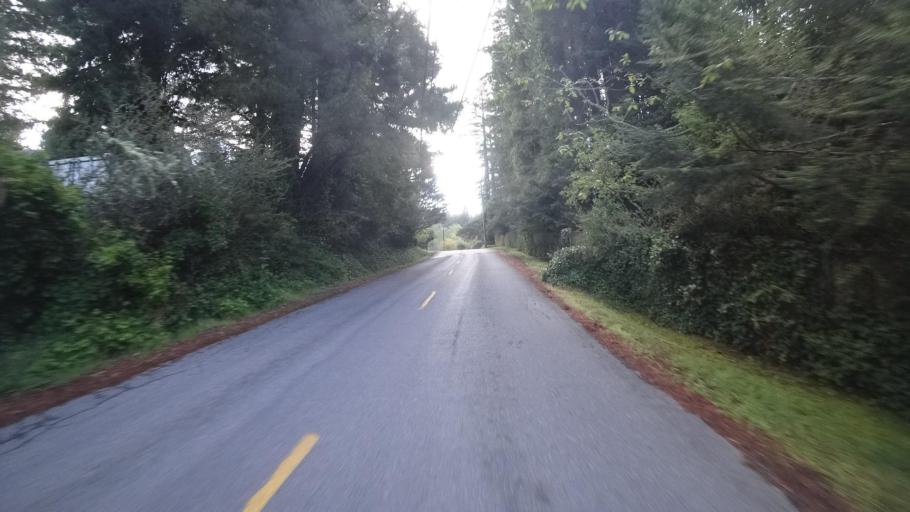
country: US
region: California
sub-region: Humboldt County
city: Westhaven-Moonstone
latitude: 41.0599
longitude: -124.1334
